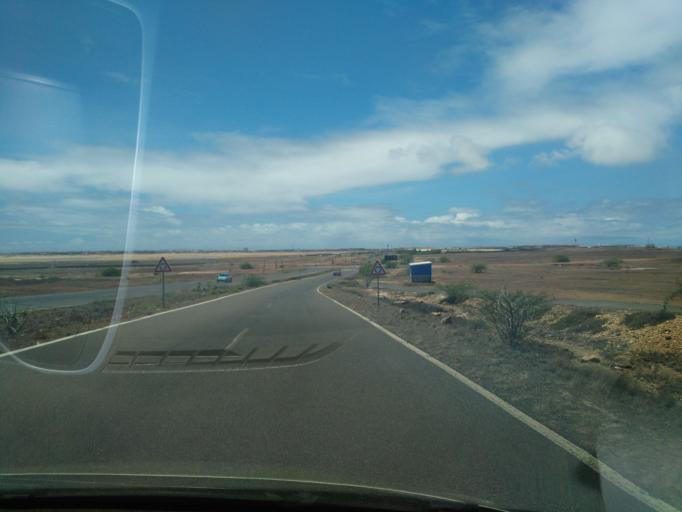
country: CV
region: Sal
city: Santa Maria
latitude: 16.6319
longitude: -22.9169
